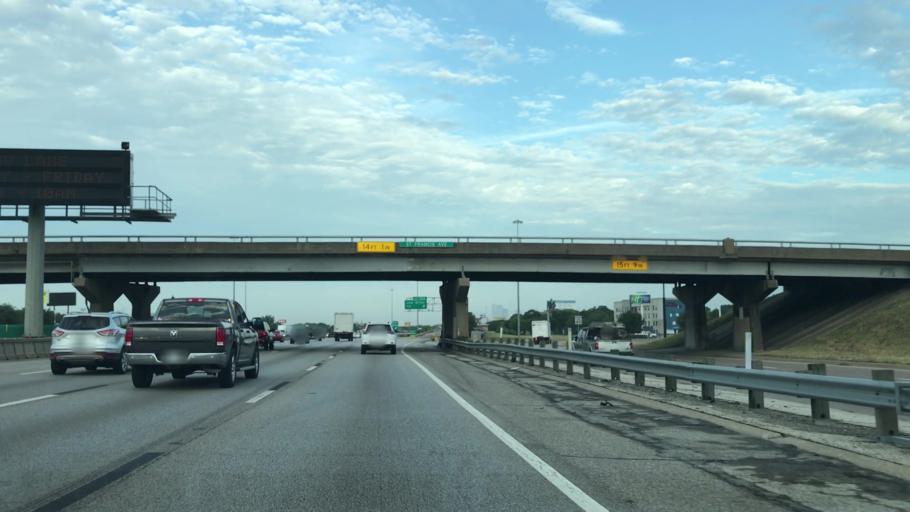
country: US
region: Texas
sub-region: Dallas County
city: Balch Springs
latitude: 32.7960
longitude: -96.6915
